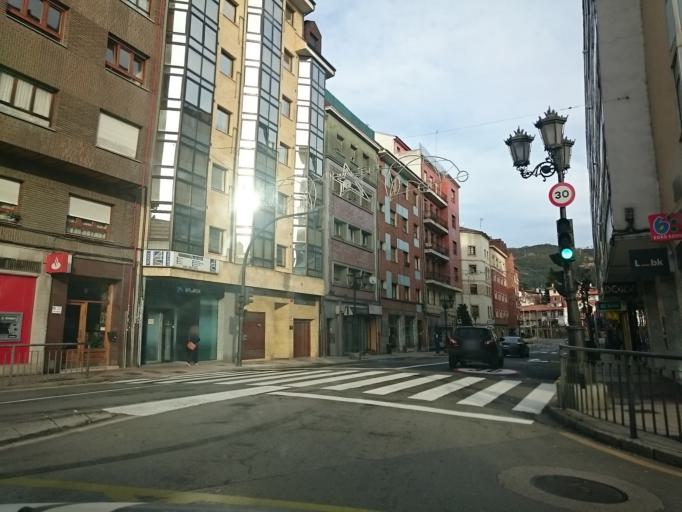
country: ES
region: Asturias
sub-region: Province of Asturias
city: Oviedo
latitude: 43.3629
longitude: -5.8583
